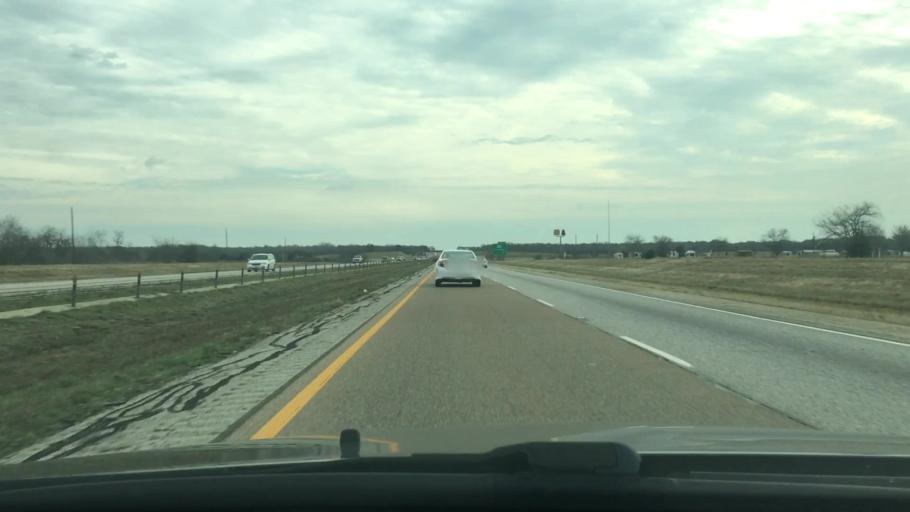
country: US
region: Texas
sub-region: Leon County
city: Centerville
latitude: 31.1000
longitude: -95.9637
